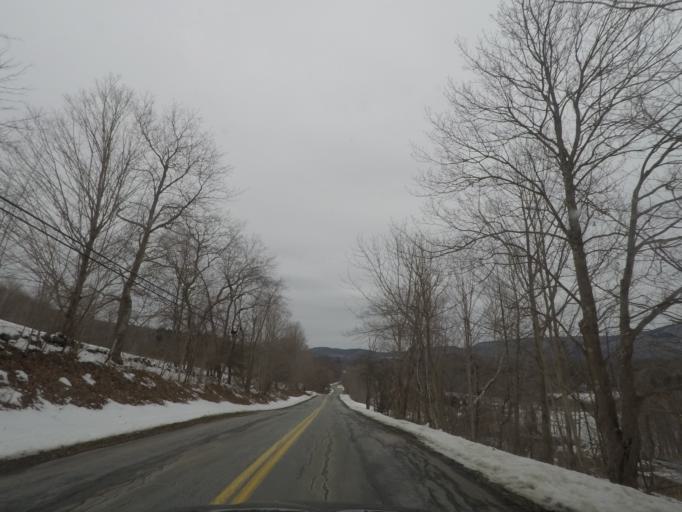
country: US
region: Massachusetts
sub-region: Berkshire County
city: Lanesborough
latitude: 42.5771
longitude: -73.3767
